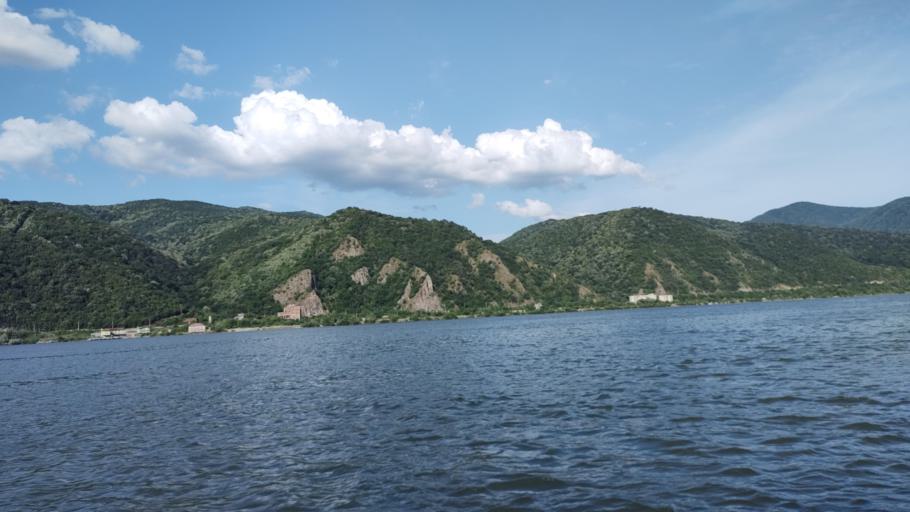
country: RO
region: Caras-Severin
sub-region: Comuna Berzasca
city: Berzasca
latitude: 44.6313
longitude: 21.9889
